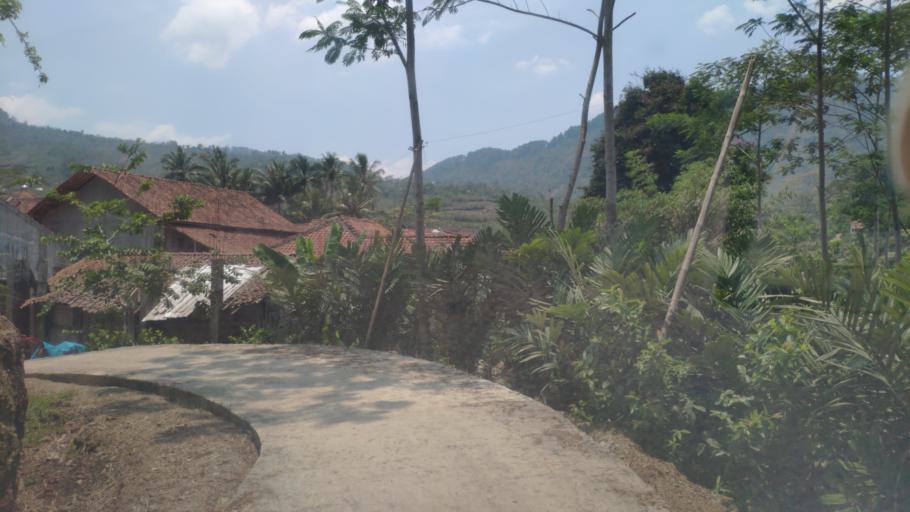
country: ID
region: Central Java
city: Wonosobo
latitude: -7.3203
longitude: 109.7476
